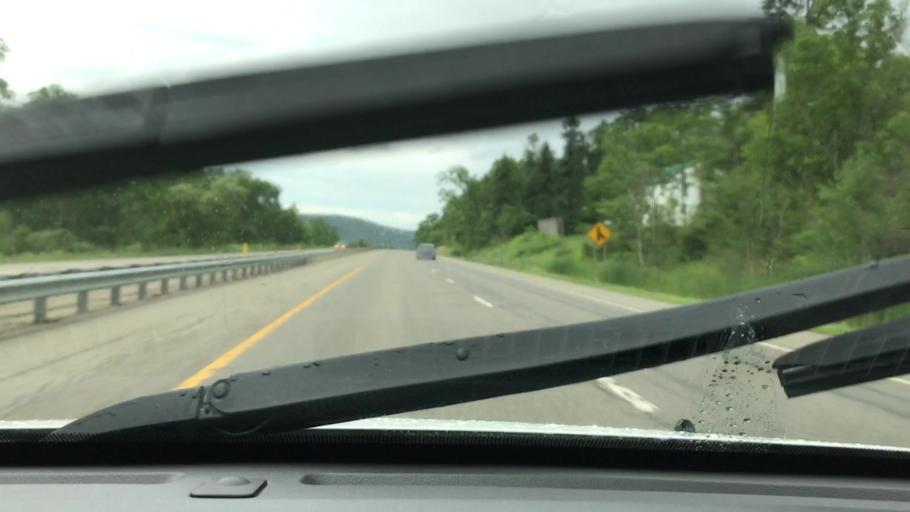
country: US
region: Pennsylvania
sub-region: McKean County
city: Foster Brook
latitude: 42.0075
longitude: -78.6223
